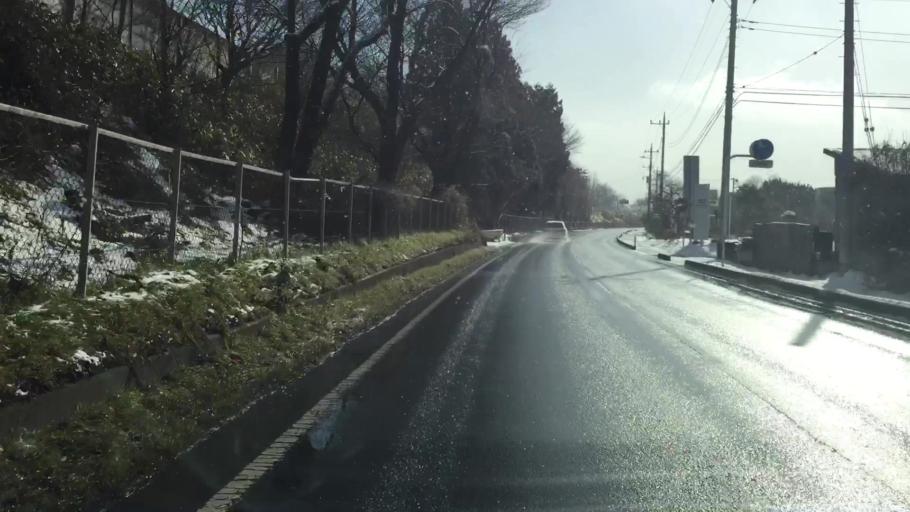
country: JP
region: Gunma
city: Numata
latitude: 36.6659
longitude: 139.0653
